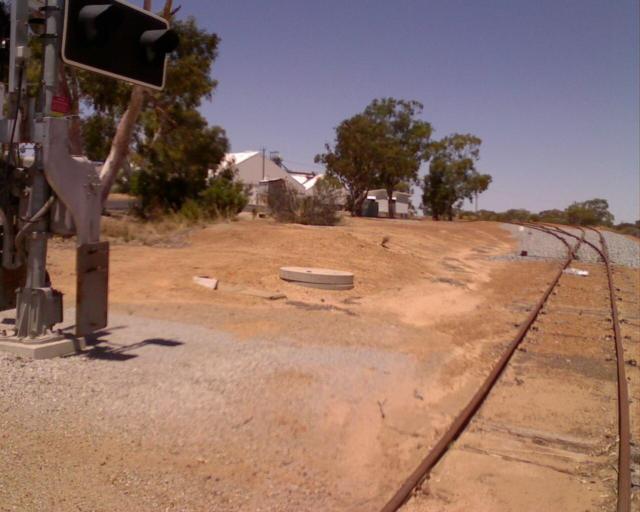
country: AU
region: Western Australia
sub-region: Merredin
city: Merredin
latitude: -30.8142
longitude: 117.8636
